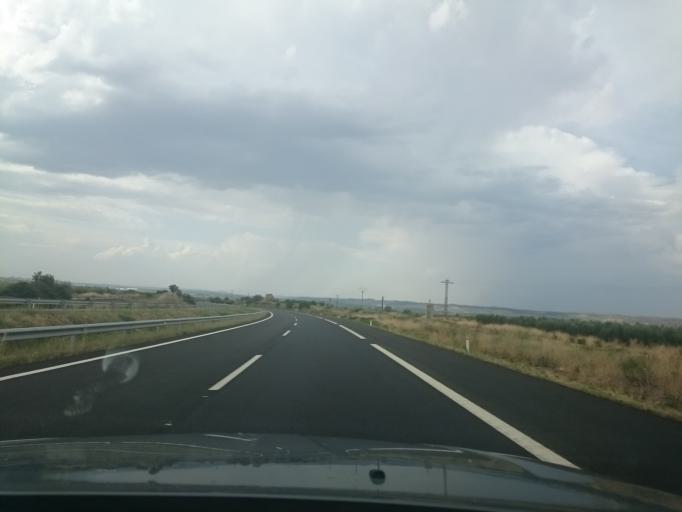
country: ES
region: La Rioja
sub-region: Provincia de La Rioja
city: Aldeanueva de Ebro
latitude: 42.2425
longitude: -1.9010
